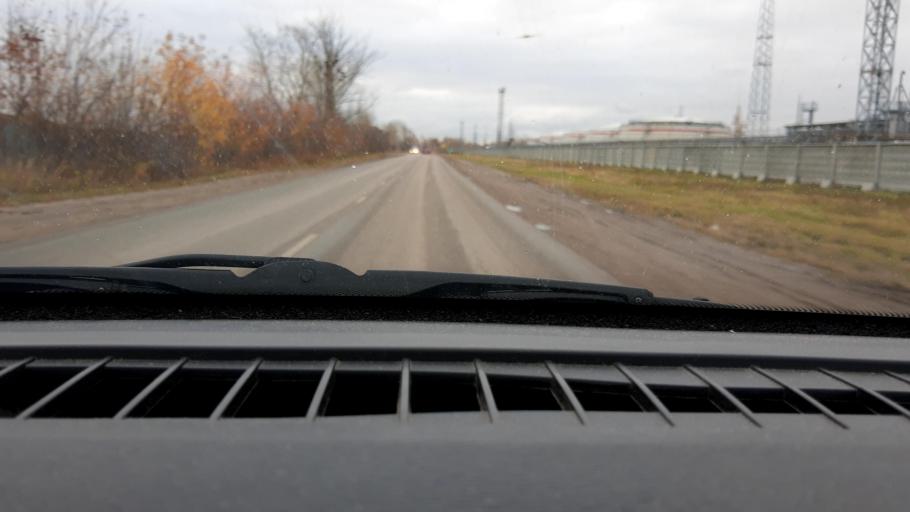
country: RU
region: Nizjnij Novgorod
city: Kstovo
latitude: 56.1208
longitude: 44.1394
